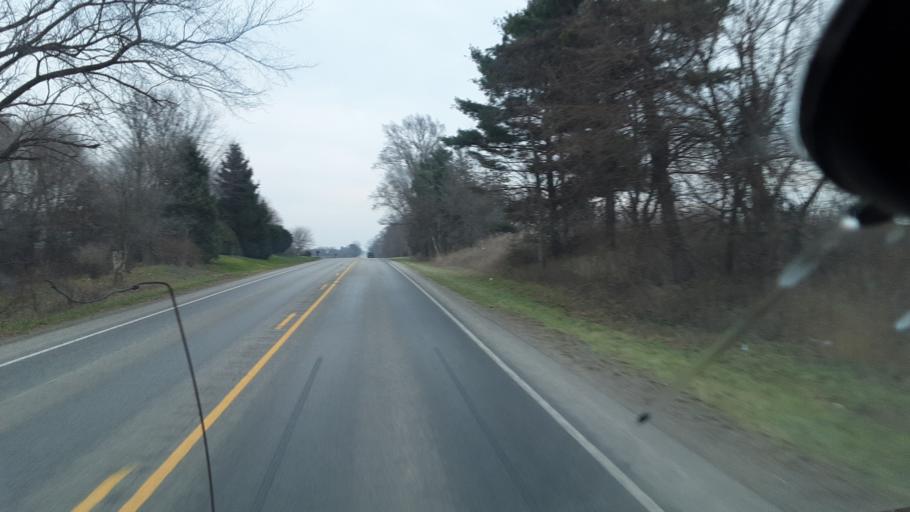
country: US
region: Michigan
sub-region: Saint Joseph County
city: White Pigeon
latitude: 41.7262
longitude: -85.6329
